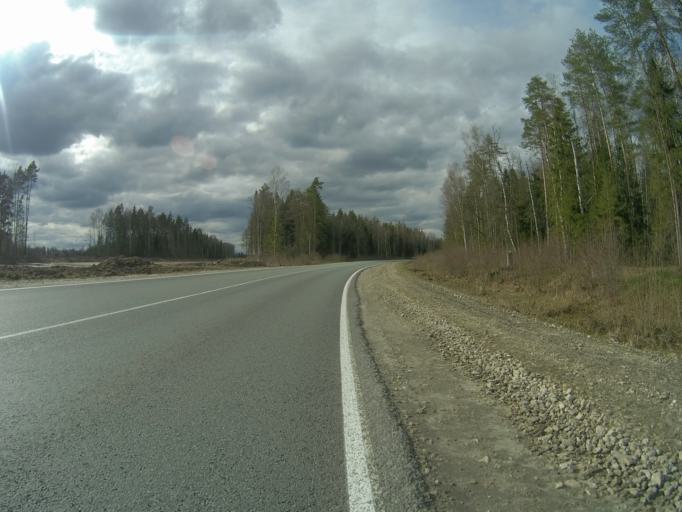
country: RU
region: Vladimir
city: Golovino
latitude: 56.0117
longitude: 40.5907
